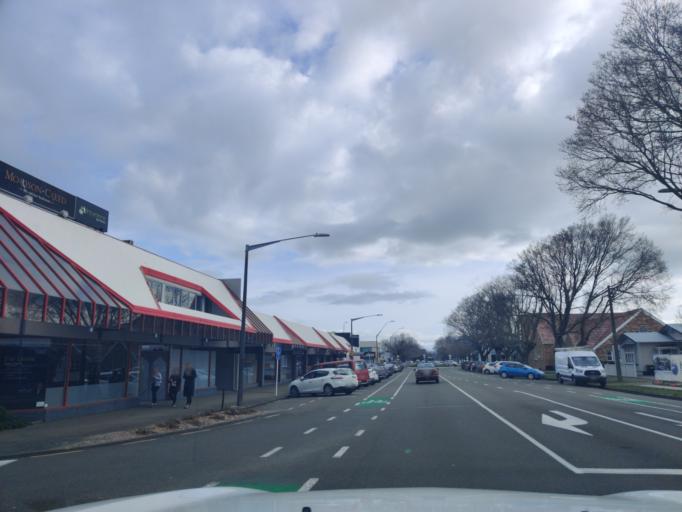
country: NZ
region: Manawatu-Wanganui
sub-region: Palmerston North City
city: Palmerston North
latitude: -40.3523
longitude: 175.6198
